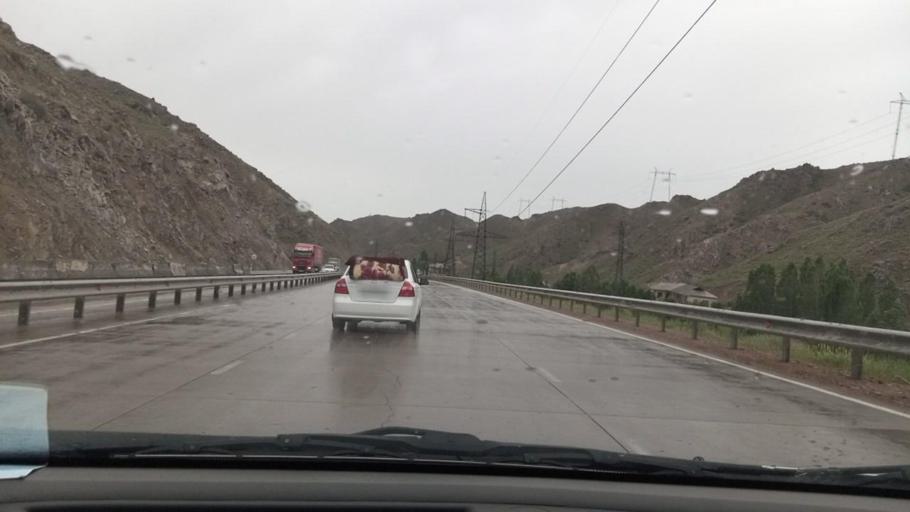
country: TJ
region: Viloyati Sughd
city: Shaydon
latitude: 40.9711
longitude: 70.6541
